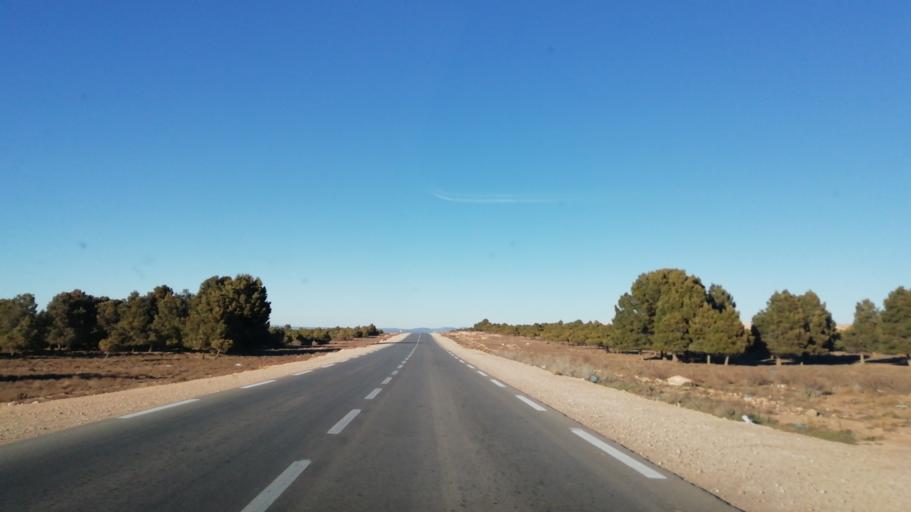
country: DZ
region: Tlemcen
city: Sebdou
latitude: 34.4416
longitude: -1.2761
